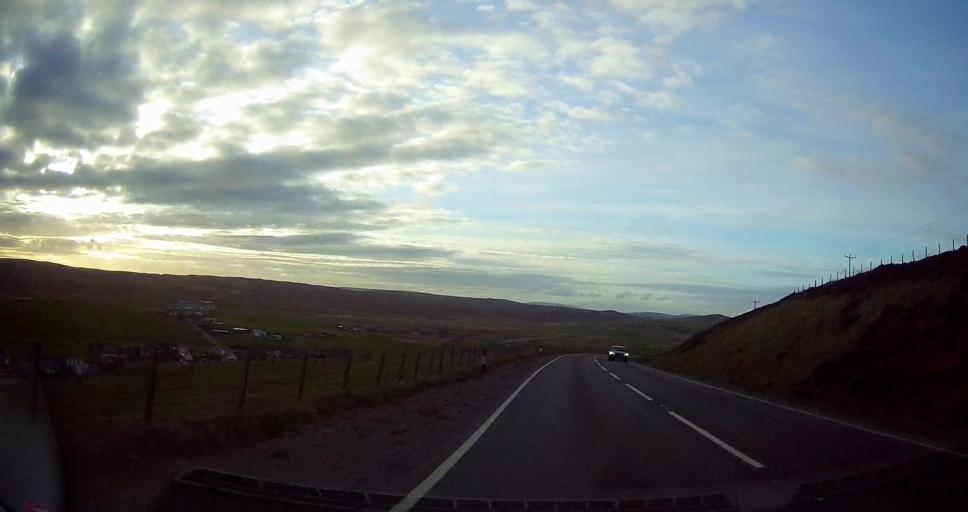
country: GB
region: Scotland
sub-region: Shetland Islands
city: Lerwick
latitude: 60.1793
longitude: -1.2250
